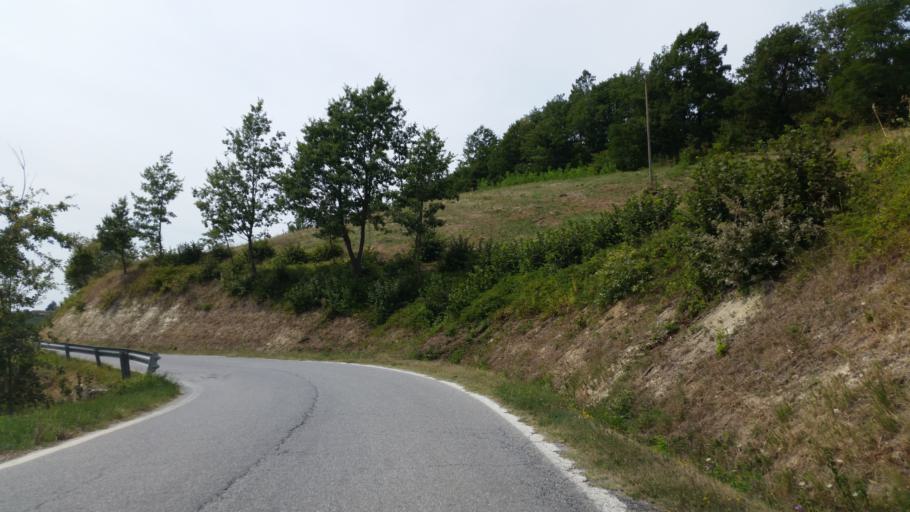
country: IT
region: Piedmont
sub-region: Provincia di Cuneo
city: Borgomale
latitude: 44.6527
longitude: 8.1315
